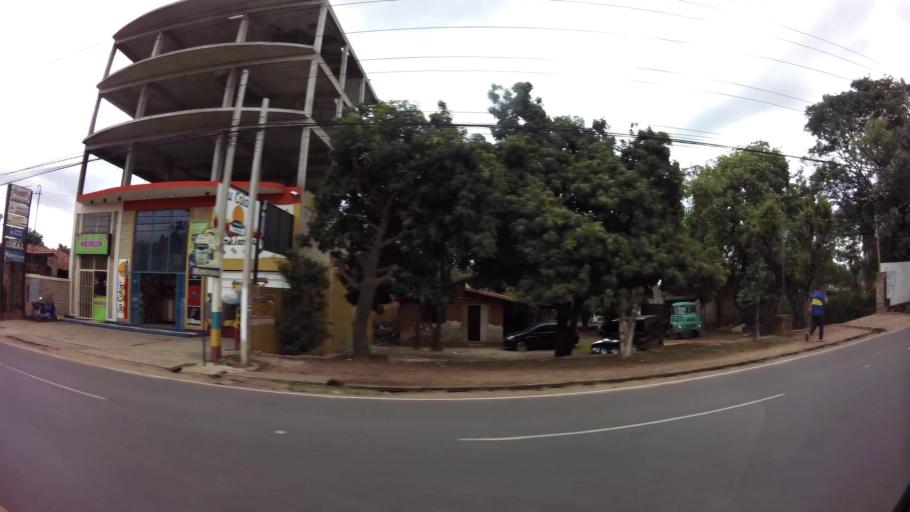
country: PY
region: Central
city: San Lorenzo
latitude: -25.2919
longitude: -57.5014
